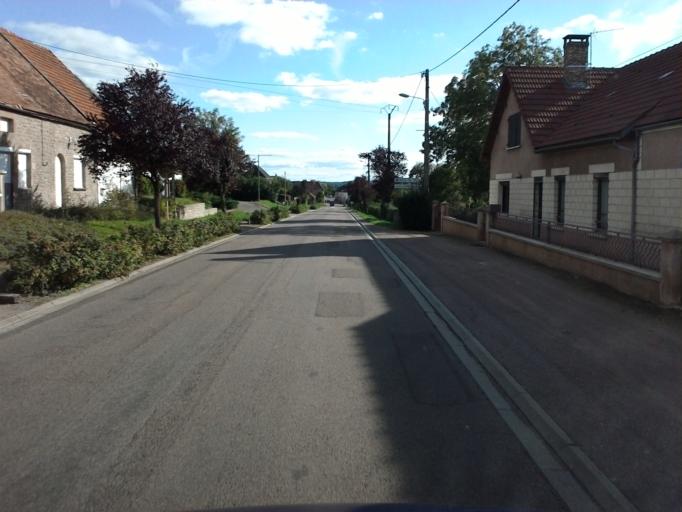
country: FR
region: Bourgogne
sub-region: Departement de la Cote-d'Or
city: Semur-en-Auxois
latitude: 47.3933
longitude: 4.3071
